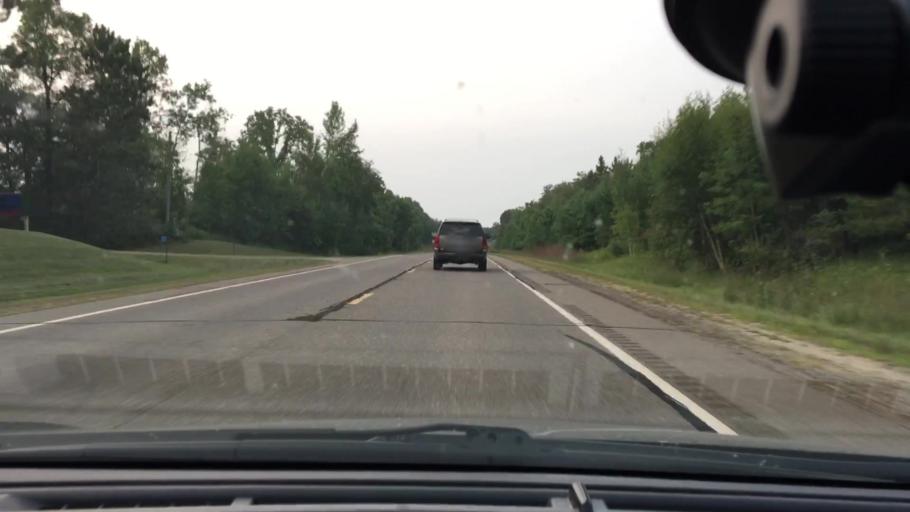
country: US
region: Minnesota
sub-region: Crow Wing County
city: Crosby
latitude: 46.4248
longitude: -93.8733
